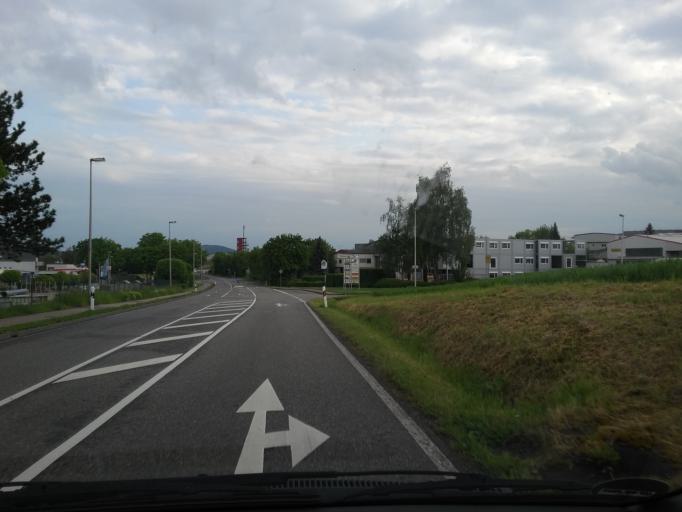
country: DE
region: Baden-Wuerttemberg
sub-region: Regierungsbezirk Stuttgart
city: Abstatt
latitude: 49.0782
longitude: 9.2909
